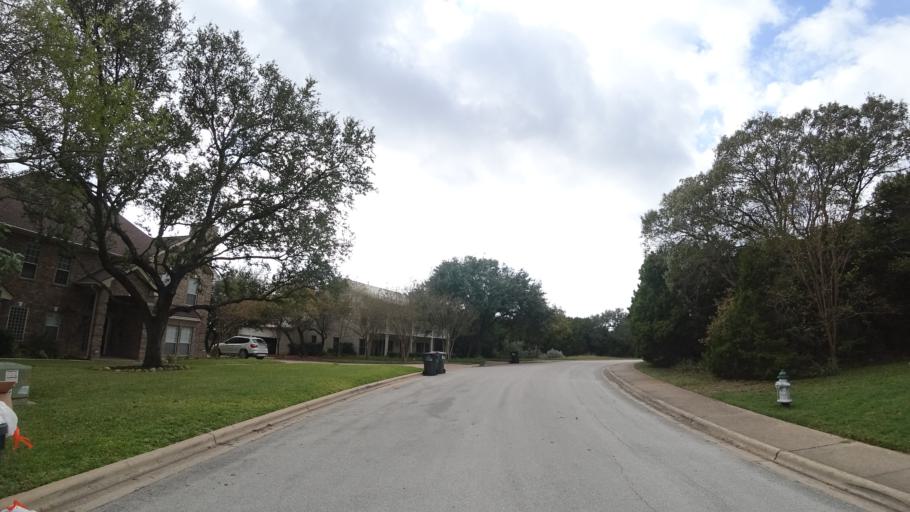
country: US
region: Texas
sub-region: Travis County
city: Barton Creek
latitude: 30.2951
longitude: -97.8843
